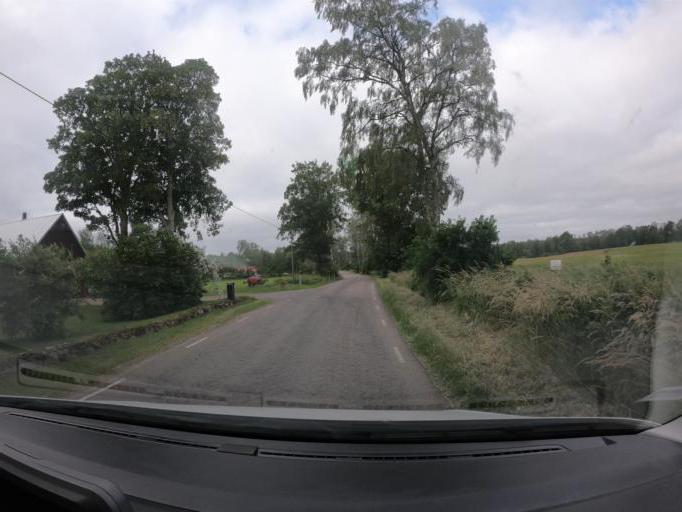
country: SE
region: Skane
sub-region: Klippans Kommun
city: Ljungbyhed
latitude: 56.0565
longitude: 13.2559
